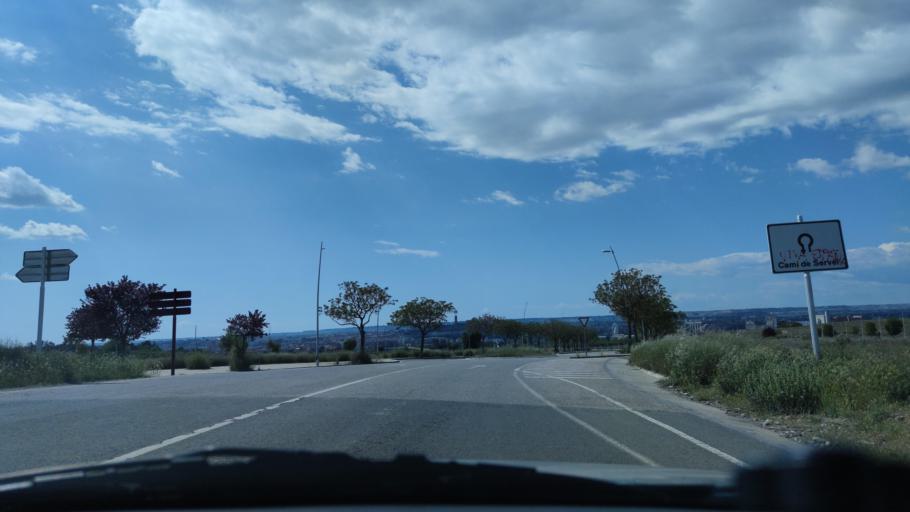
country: ES
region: Catalonia
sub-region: Provincia de Lleida
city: Lleida
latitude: 41.6027
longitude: 0.6639
